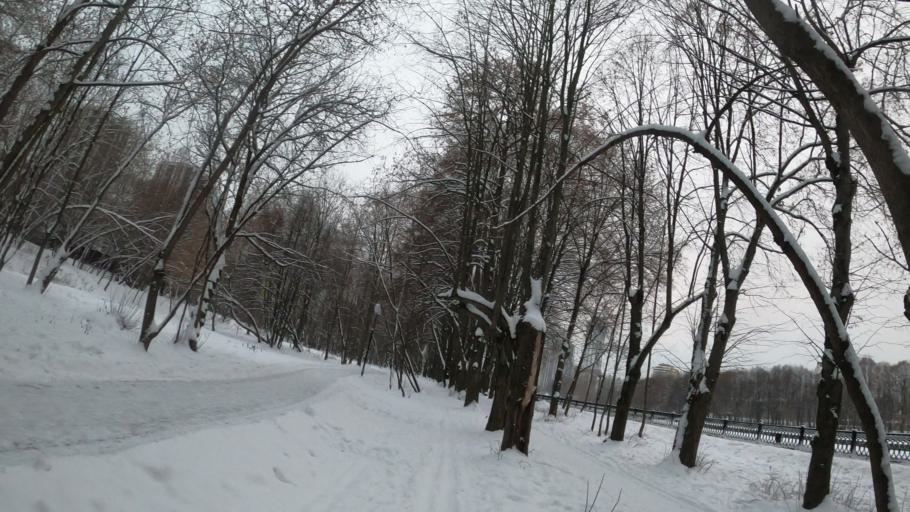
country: RU
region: Moskovskaya
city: Levoberezhnaya
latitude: 55.9044
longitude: 37.4713
